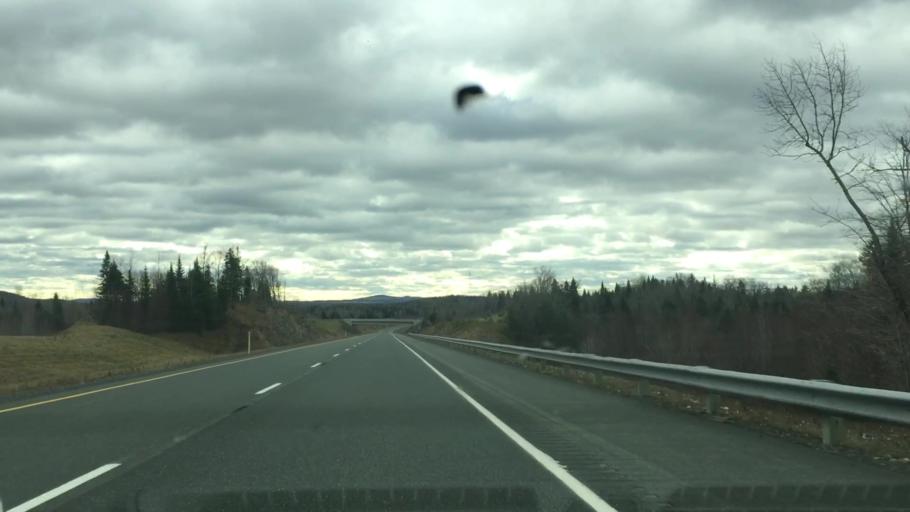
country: US
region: Maine
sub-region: Aroostook County
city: Easton
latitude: 46.6307
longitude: -67.7417
